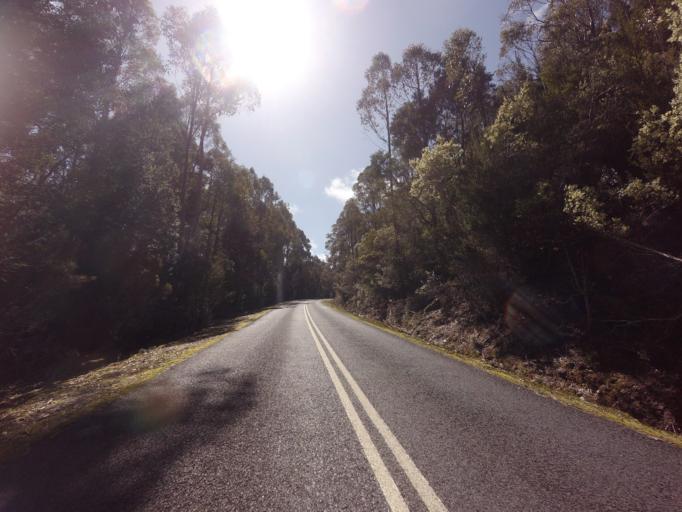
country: AU
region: Tasmania
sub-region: Derwent Valley
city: New Norfolk
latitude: -42.7225
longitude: 146.4370
